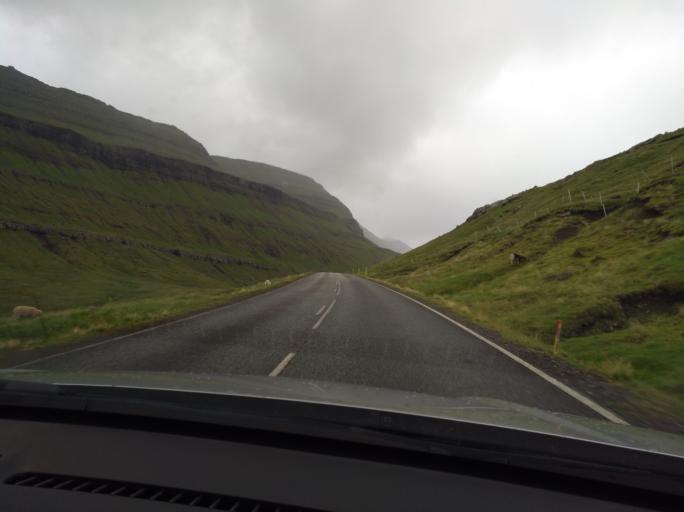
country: FO
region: Eysturoy
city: Fuglafjordur
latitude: 62.2298
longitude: -6.8791
